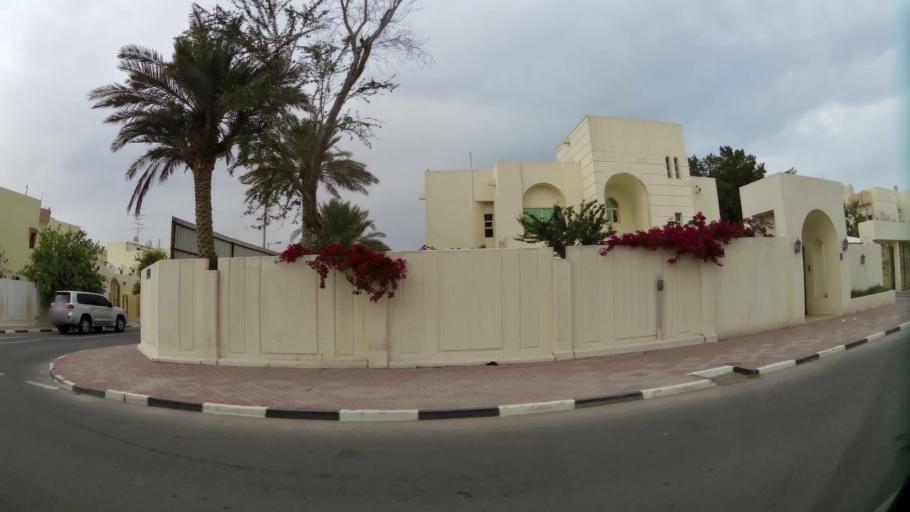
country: QA
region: Baladiyat ad Dawhah
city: Doha
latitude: 25.3328
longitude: 51.5084
